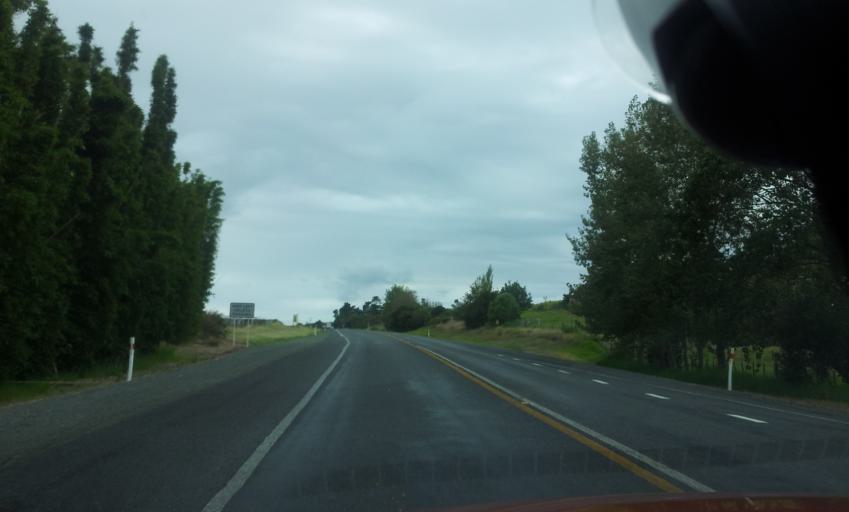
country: NZ
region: Northland
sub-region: Whangarei
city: Ruakaka
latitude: -35.9554
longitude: 174.4517
